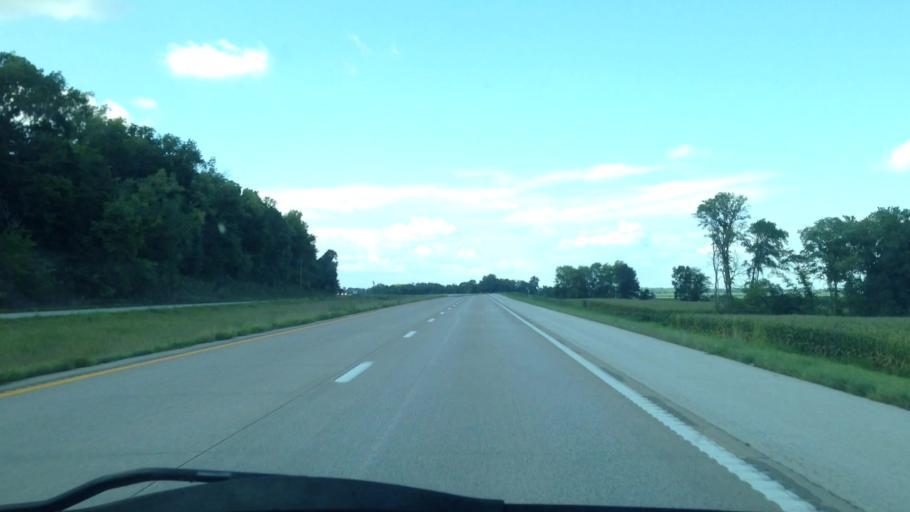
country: US
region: Missouri
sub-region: Lewis County
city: Canton
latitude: 40.2193
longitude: -91.5261
